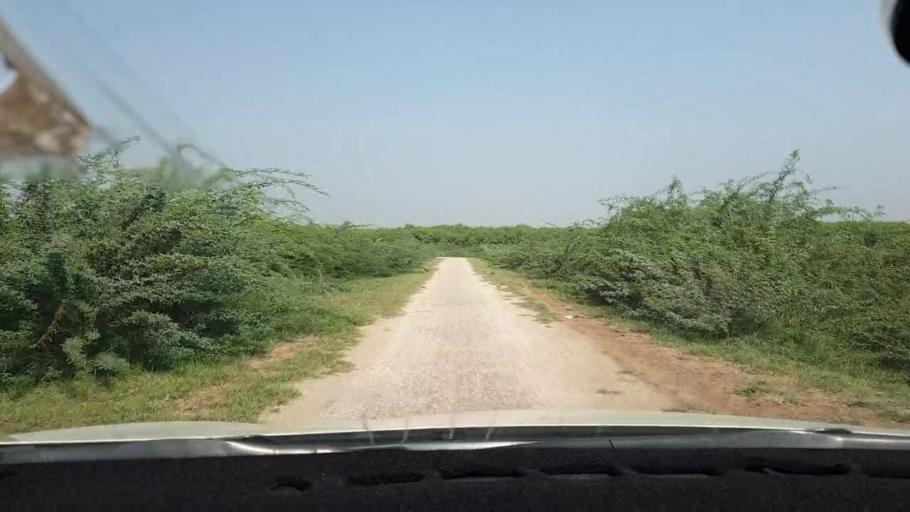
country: PK
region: Sindh
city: Tando Mittha Khan
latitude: 25.9435
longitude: 69.2989
